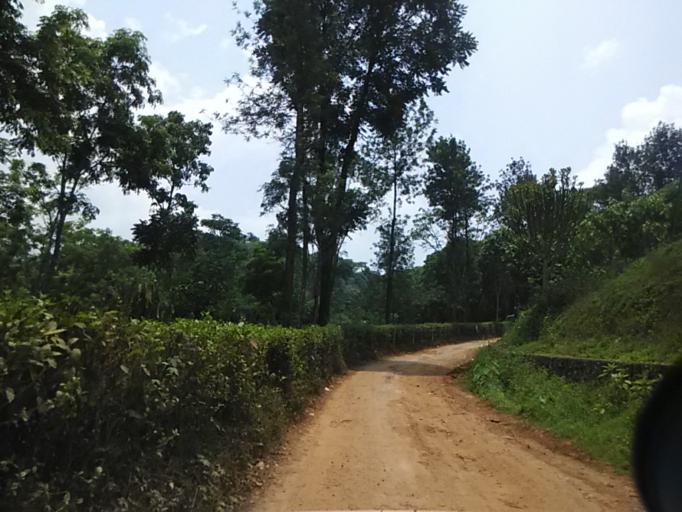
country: IN
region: Karnataka
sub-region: Kodagu
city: Virarajendrapet
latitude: 12.2084
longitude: 75.6737
